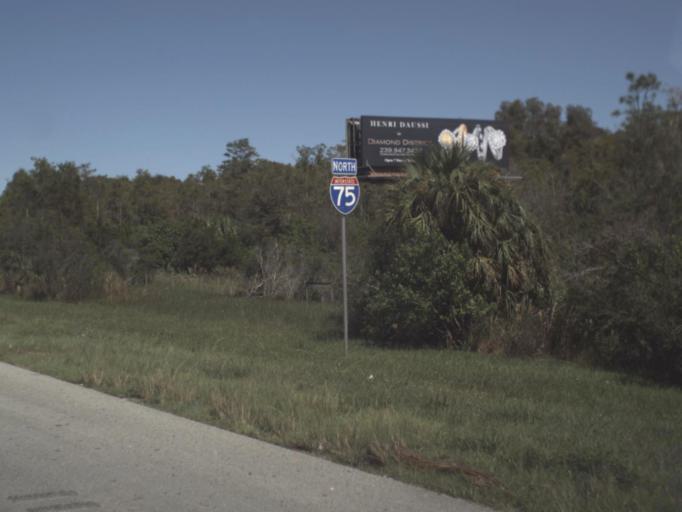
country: US
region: Florida
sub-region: Lee County
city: Tice
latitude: 26.6427
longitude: -81.8003
